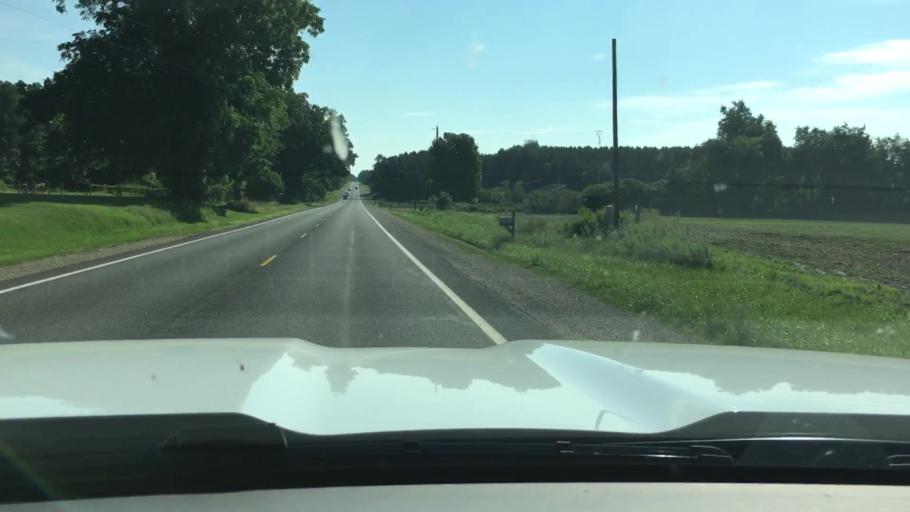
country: US
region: Michigan
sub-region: Montcalm County
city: Edmore
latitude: 43.4084
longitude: -84.8821
